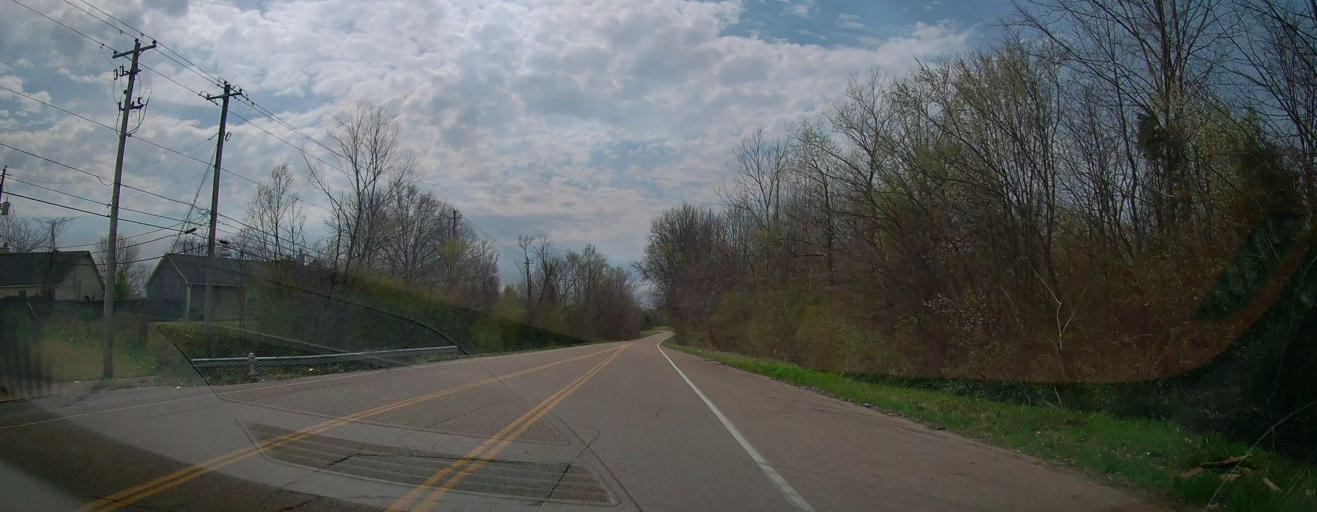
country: US
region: Mississippi
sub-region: De Soto County
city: Olive Branch
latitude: 35.0051
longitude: -89.8485
